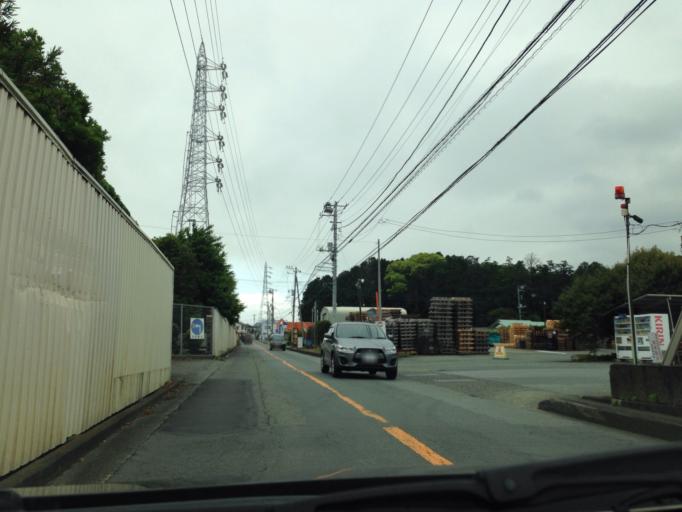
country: JP
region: Shizuoka
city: Mishima
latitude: 35.1615
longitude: 138.9104
